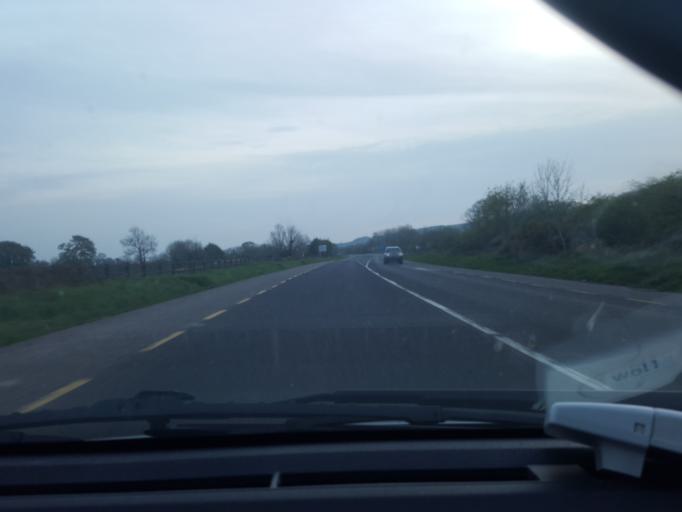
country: IE
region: Munster
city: Cahir
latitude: 52.3570
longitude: -7.9919
